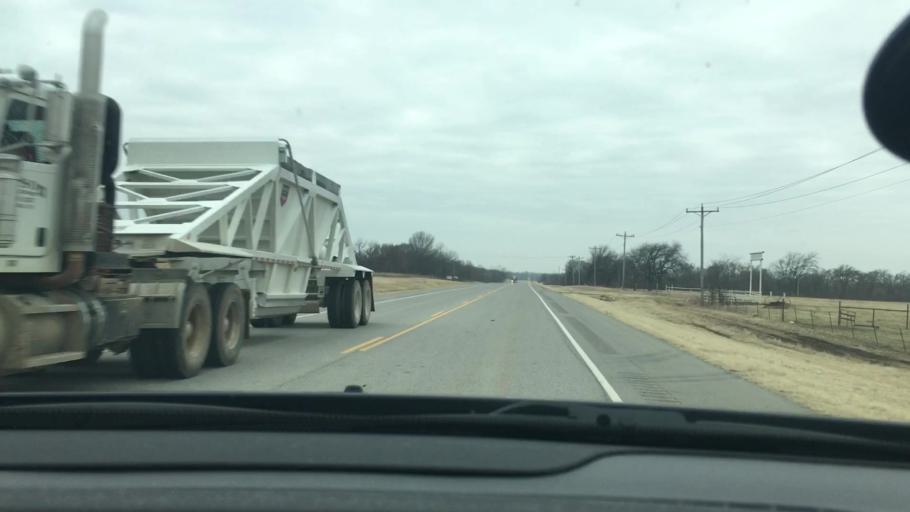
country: US
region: Oklahoma
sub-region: Carter County
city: Healdton
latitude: 34.4924
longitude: -97.4229
